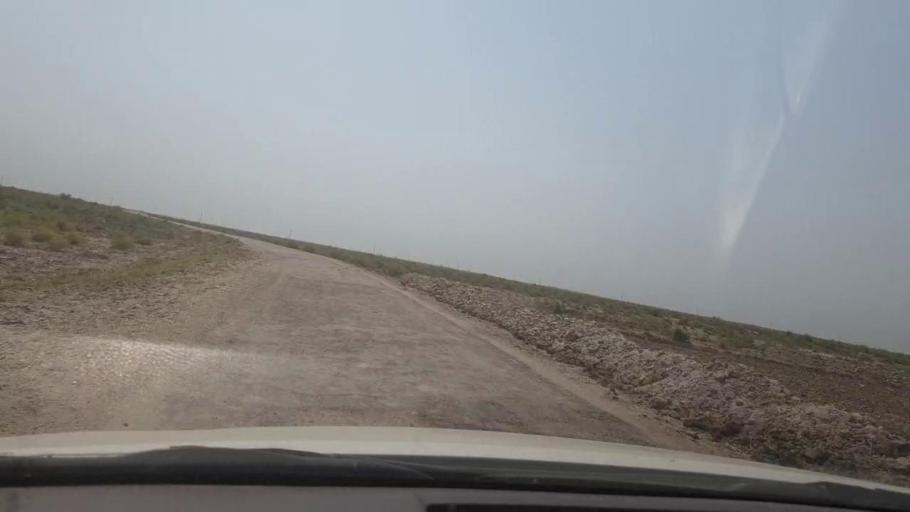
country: PK
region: Sindh
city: Garhi Yasin
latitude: 27.9889
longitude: 68.5089
